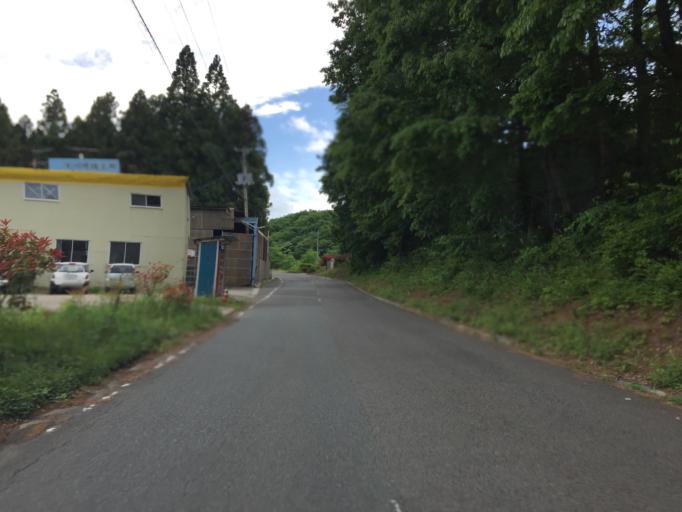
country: JP
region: Fukushima
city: Nihommatsu
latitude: 37.6357
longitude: 140.5035
